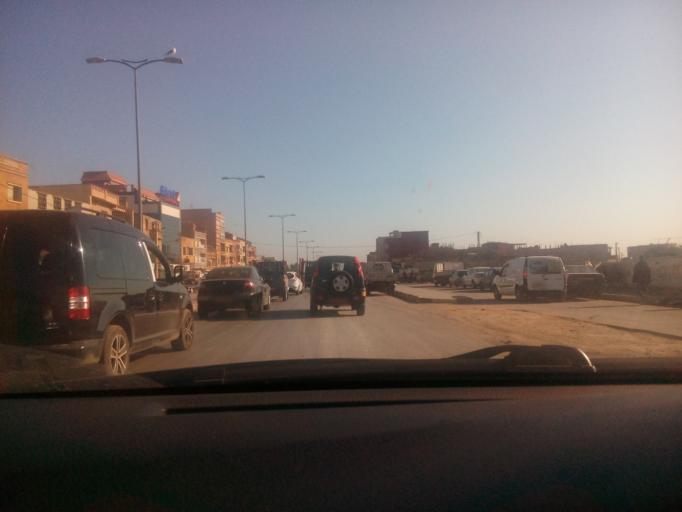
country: DZ
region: Oran
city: Oran
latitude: 35.6609
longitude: -0.6921
